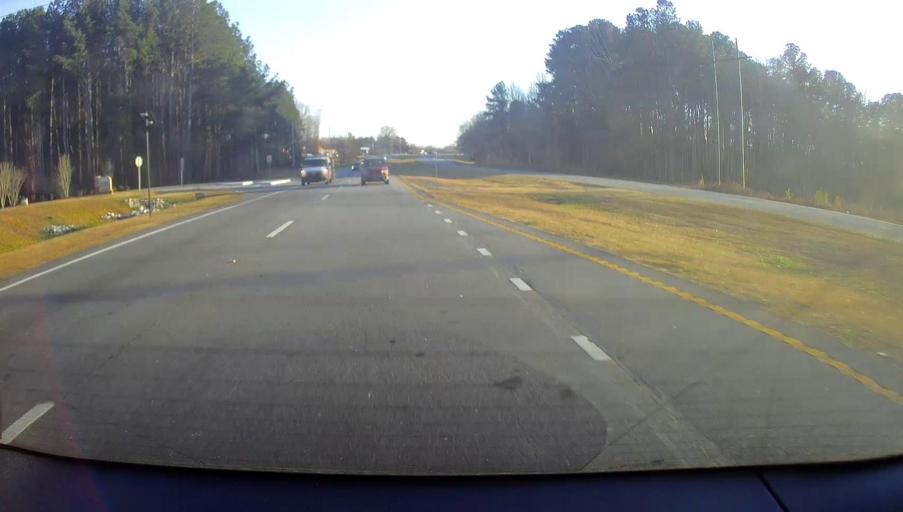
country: US
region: Georgia
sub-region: Fulton County
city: Fairburn
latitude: 33.5328
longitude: -84.5767
